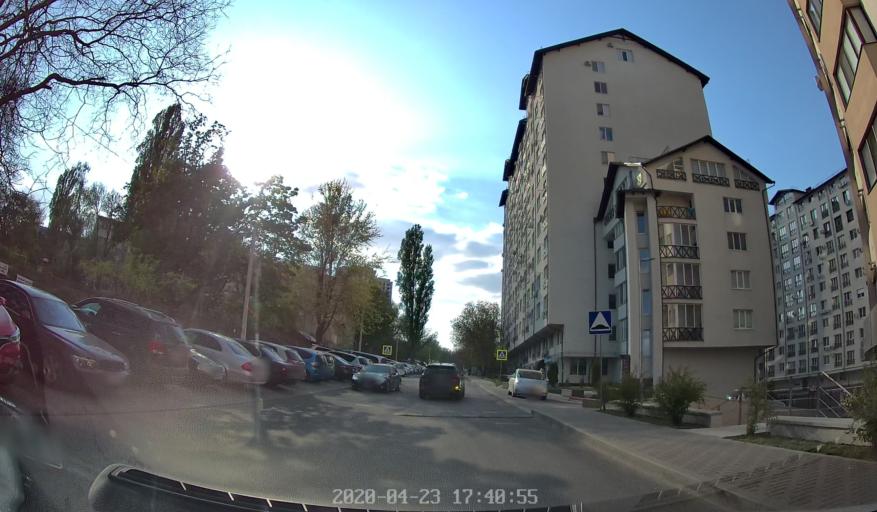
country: MD
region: Chisinau
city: Chisinau
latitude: 46.9866
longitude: 28.8413
